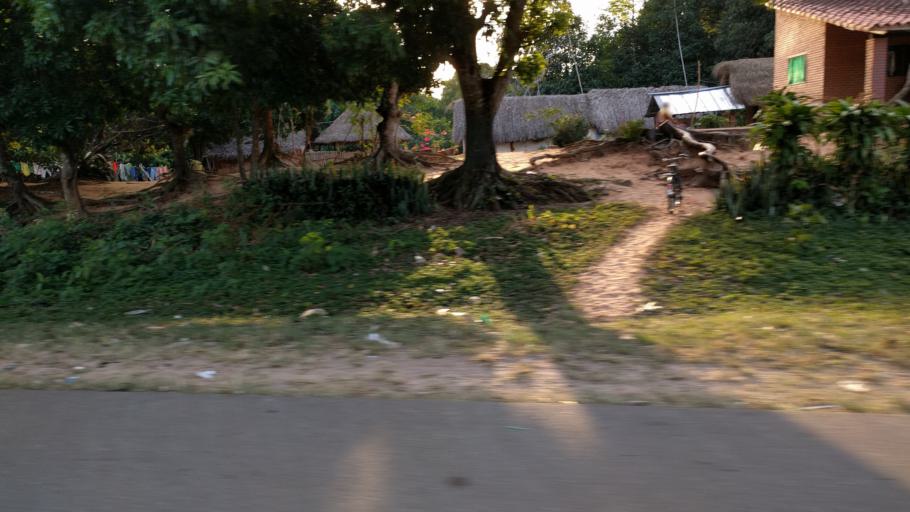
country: BO
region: Santa Cruz
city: Buena Vista
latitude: -17.4132
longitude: -63.6158
